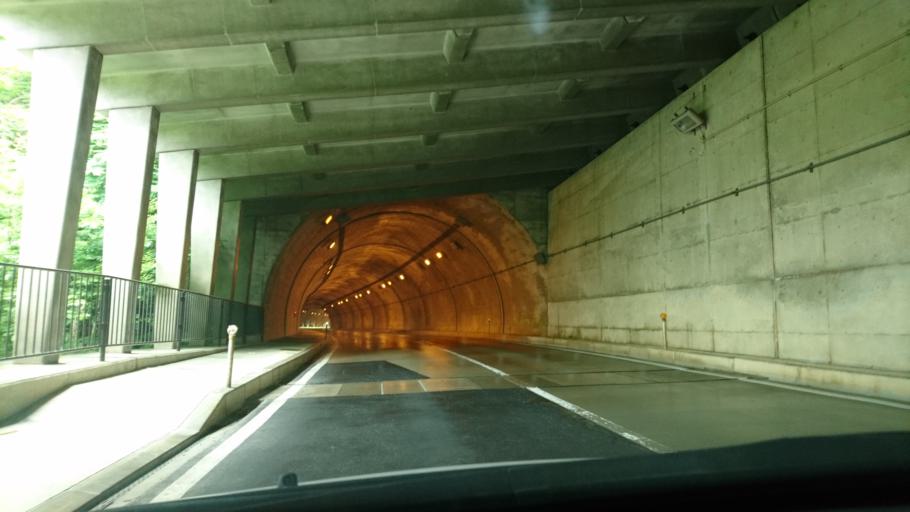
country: JP
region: Iwate
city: Mizusawa
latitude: 39.1257
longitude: 140.9171
